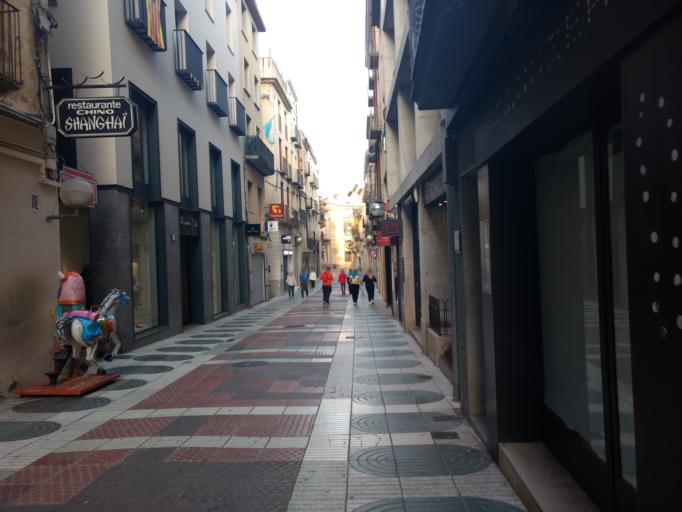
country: ES
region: Catalonia
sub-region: Provincia de Girona
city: Figueres
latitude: 42.2676
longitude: 2.9611
